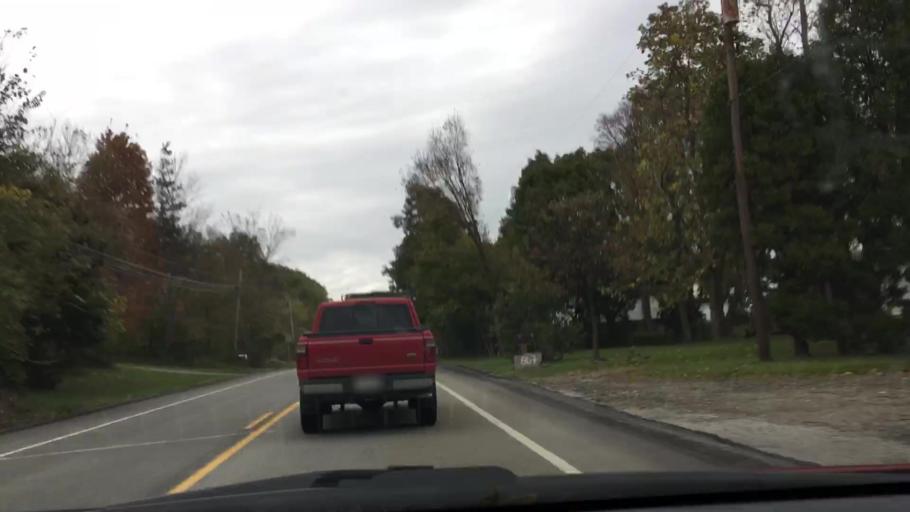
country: US
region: Pennsylvania
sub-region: Armstrong County
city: Orchard Hills
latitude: 40.5848
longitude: -79.5424
